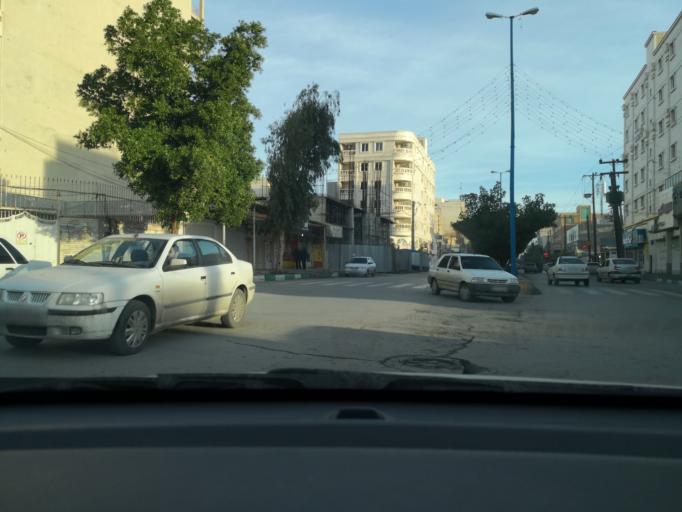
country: IR
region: Khuzestan
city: Ahvaz
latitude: 31.3536
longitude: 48.6775
